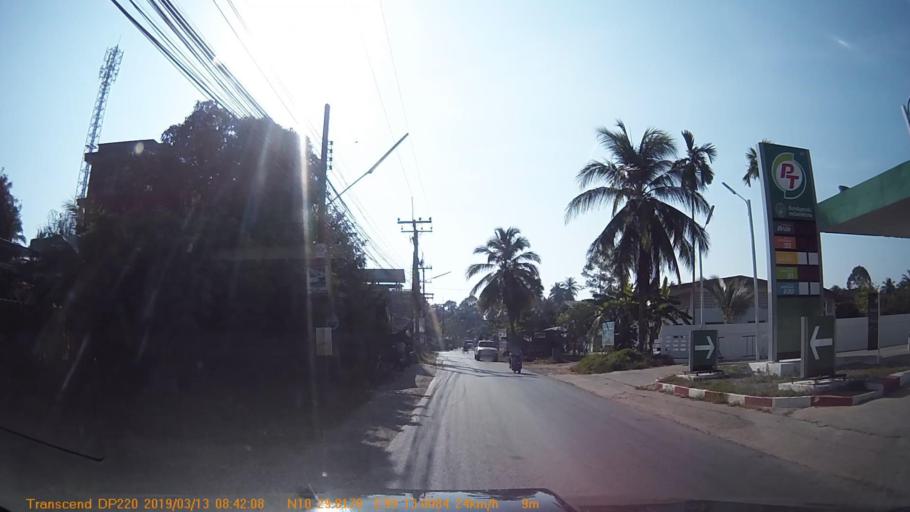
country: TH
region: Chumphon
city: Chumphon
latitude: 10.4969
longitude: 99.2169
